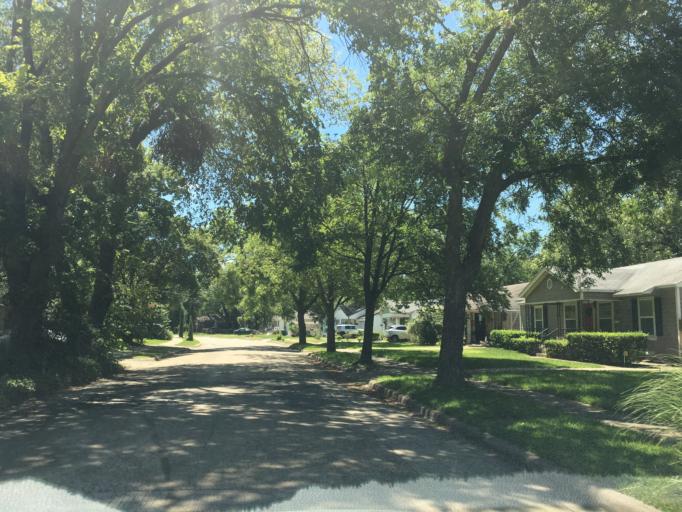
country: US
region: Texas
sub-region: Dallas County
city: Garland
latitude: 32.8422
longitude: -96.6882
